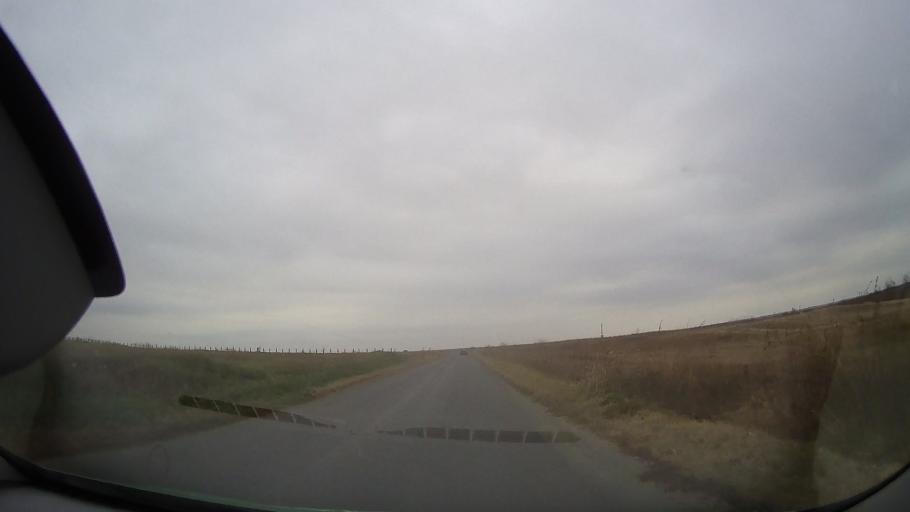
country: RO
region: Buzau
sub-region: Comuna Rusetu
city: Rusetu
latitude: 44.9655
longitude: 27.2026
